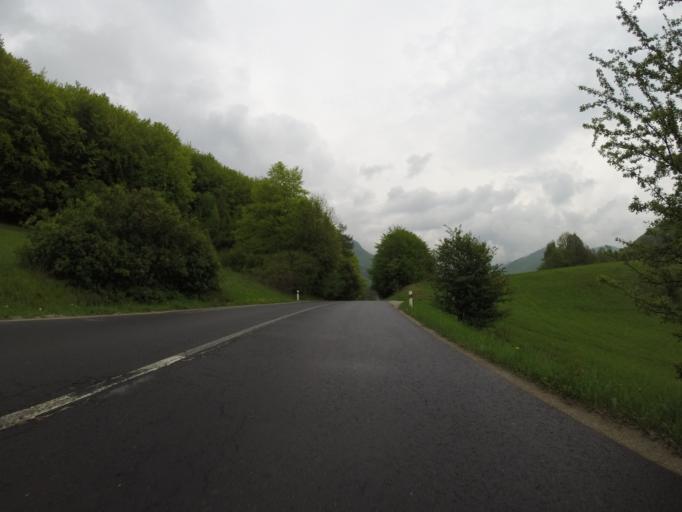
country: SK
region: Banskobystricky
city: Revuca
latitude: 48.7349
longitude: 20.0361
